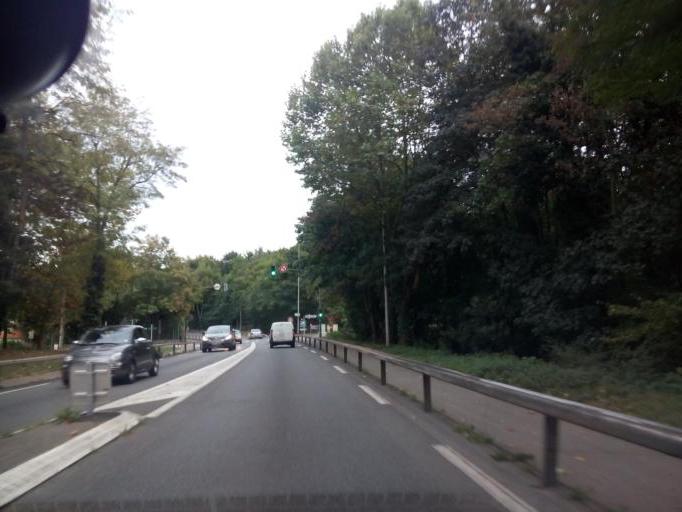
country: FR
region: Rhone-Alpes
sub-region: Departement du Rhone
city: Ecully
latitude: 45.7656
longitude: 4.7715
